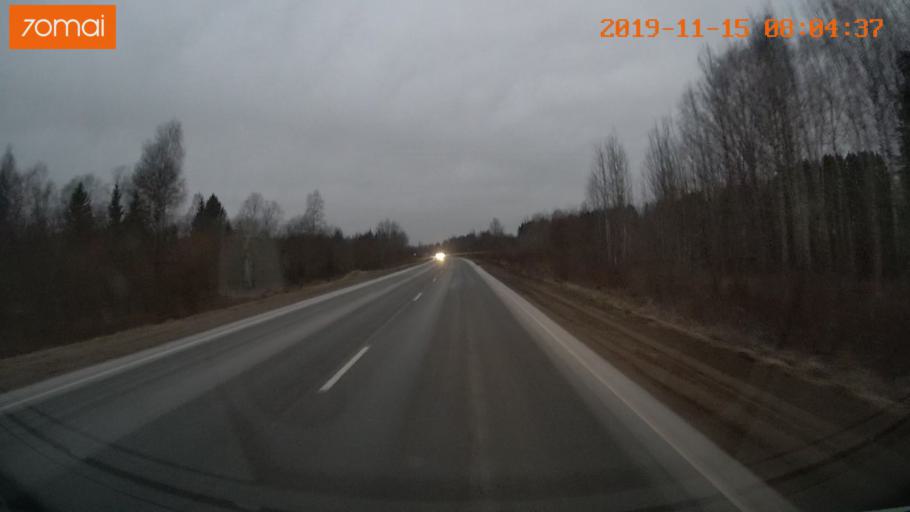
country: RU
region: Vologda
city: Cherepovets
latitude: 59.0099
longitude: 38.0731
